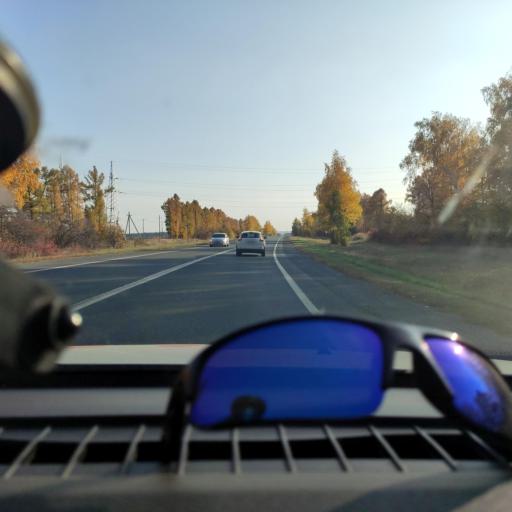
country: RU
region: Samara
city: Volzhskiy
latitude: 53.4652
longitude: 50.1278
